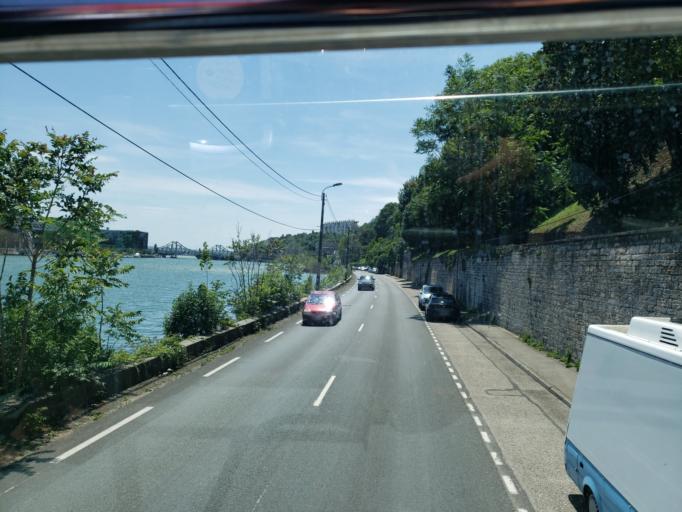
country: FR
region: Rhone-Alpes
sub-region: Departement du Rhone
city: La Mulatiere
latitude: 45.7391
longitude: 4.8119
